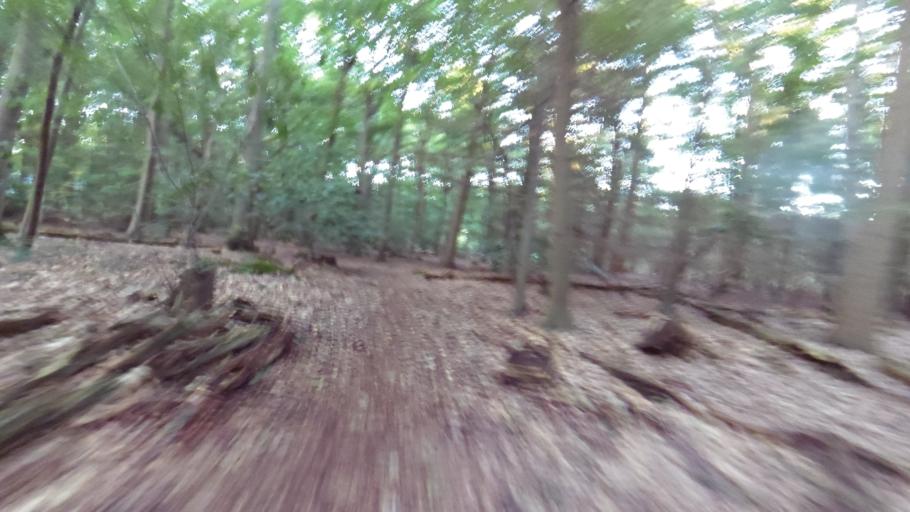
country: NL
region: Utrecht
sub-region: Gemeente Zeist
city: Zeist
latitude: 52.1243
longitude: 5.2510
